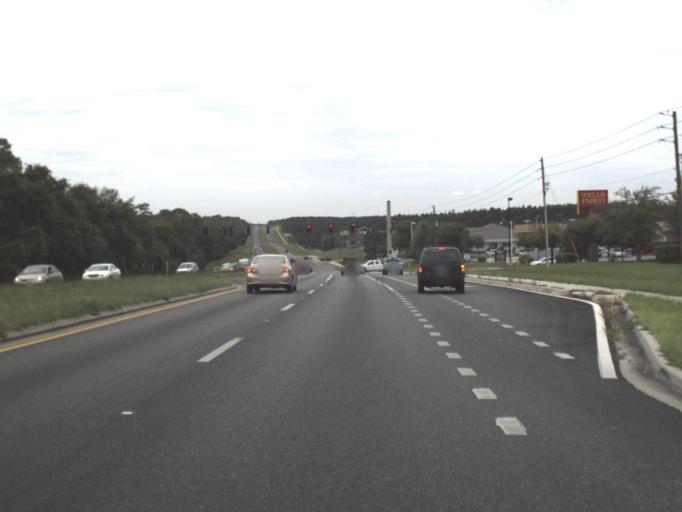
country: US
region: Florida
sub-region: Citrus County
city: Inverness Highlands North
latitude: 28.8549
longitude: -82.3924
